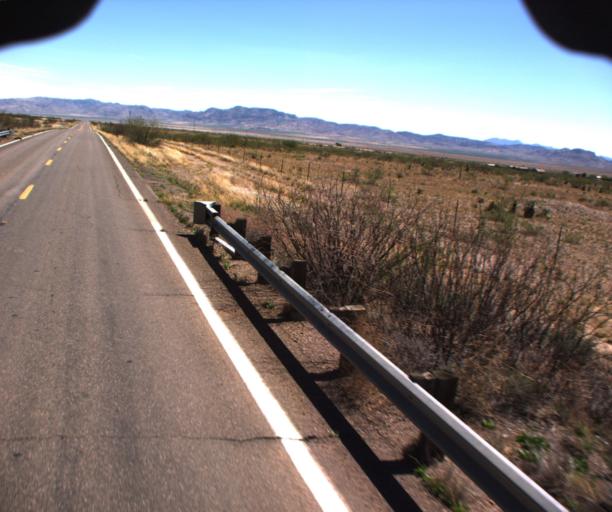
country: US
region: Arizona
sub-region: Cochise County
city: Douglas
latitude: 31.6357
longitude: -109.1882
